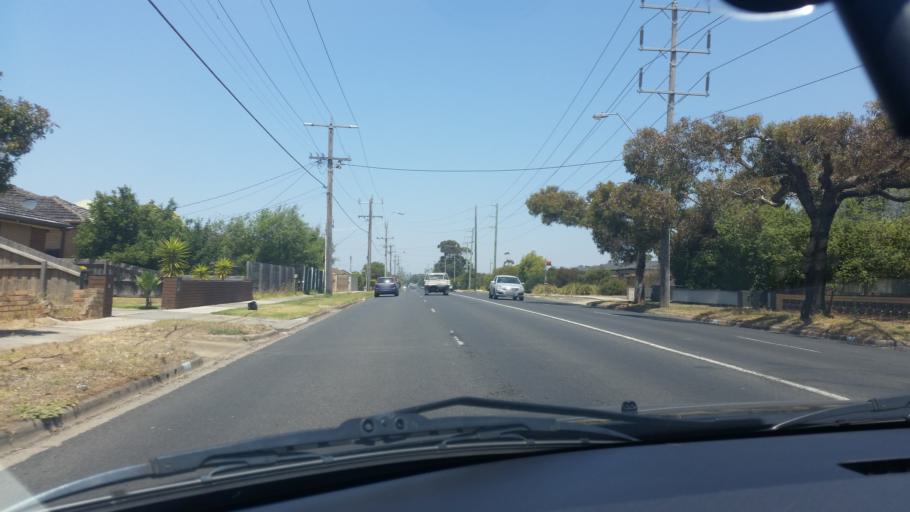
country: AU
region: Victoria
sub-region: Greater Geelong
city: Bell Park
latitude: -38.1160
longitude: 144.3424
